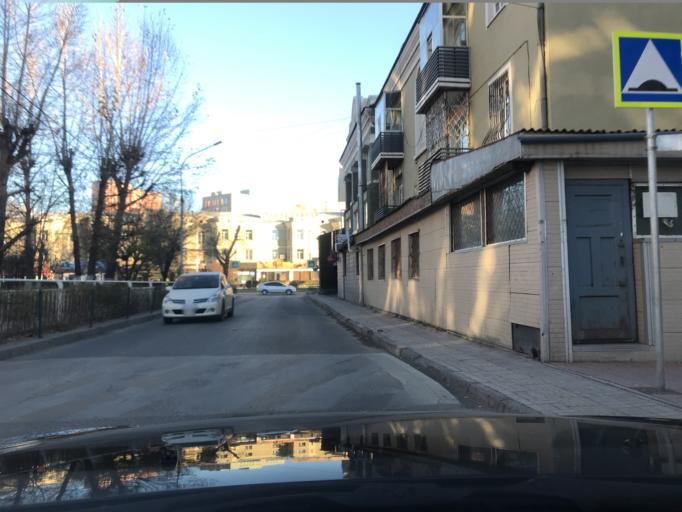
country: MN
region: Ulaanbaatar
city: Ulaanbaatar
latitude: 47.9247
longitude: 106.9108
